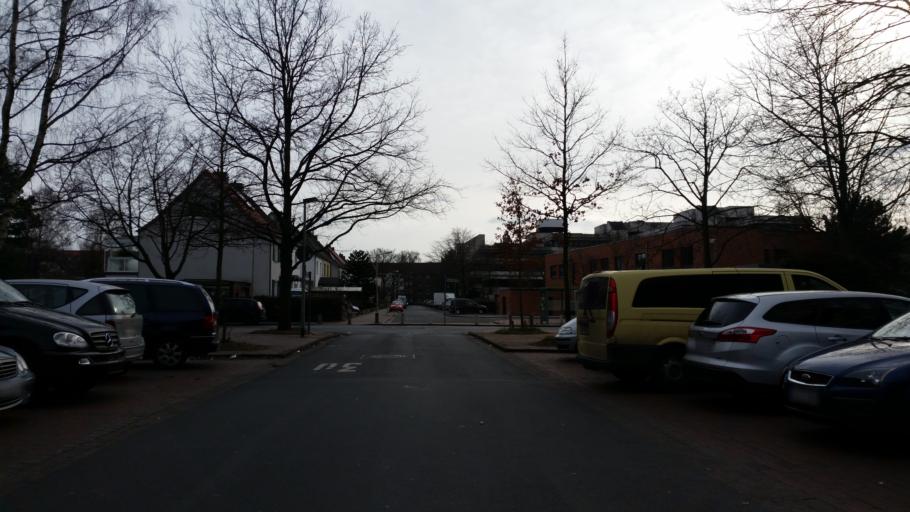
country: DE
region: Lower Saxony
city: Hannover
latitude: 52.4043
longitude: 9.7769
